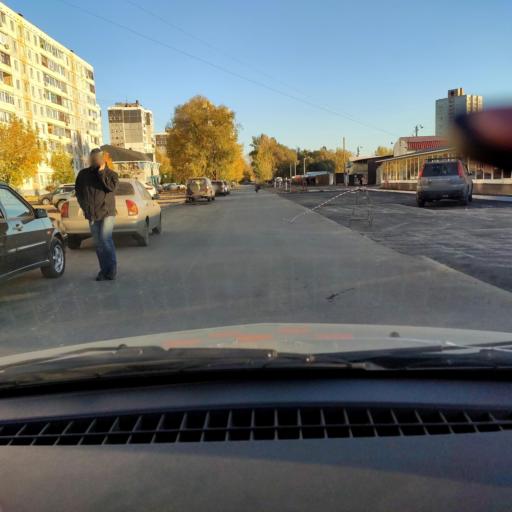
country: RU
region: Bashkortostan
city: Ufa
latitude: 54.7678
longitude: 56.0731
